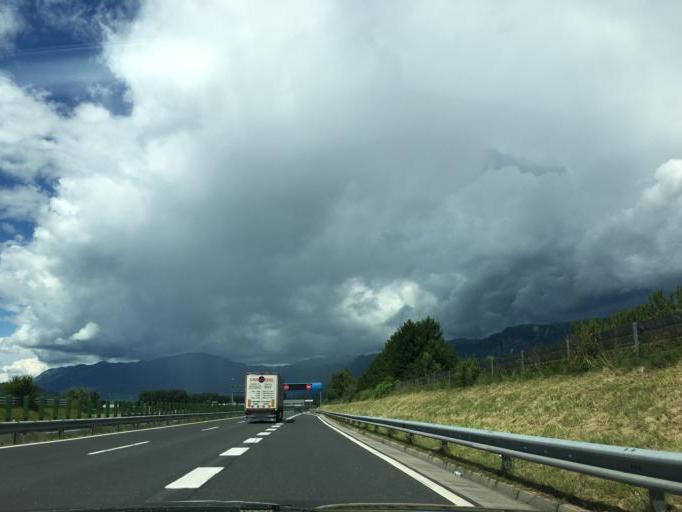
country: SI
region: Vipava
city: Vipava
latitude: 45.8309
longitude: 13.9572
